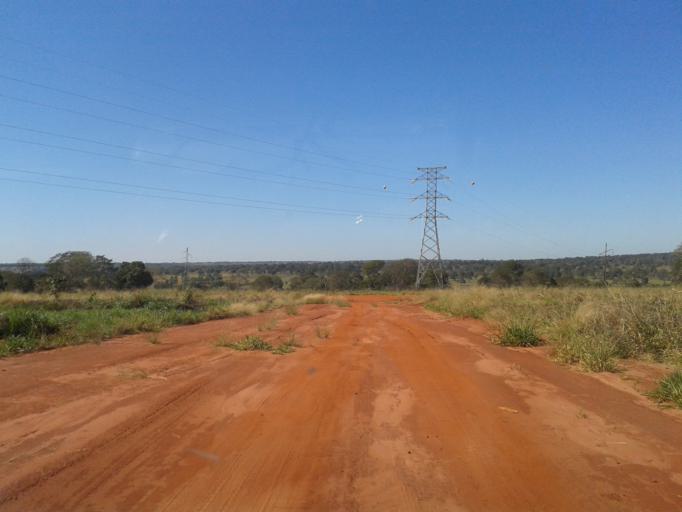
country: BR
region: Minas Gerais
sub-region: Santa Vitoria
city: Santa Vitoria
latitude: -18.8614
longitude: -50.1180
